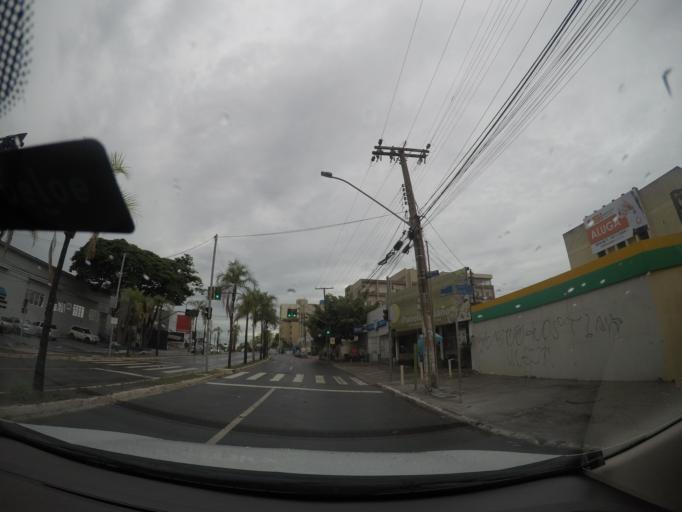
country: BR
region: Goias
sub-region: Goiania
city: Goiania
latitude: -16.6952
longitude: -49.2517
